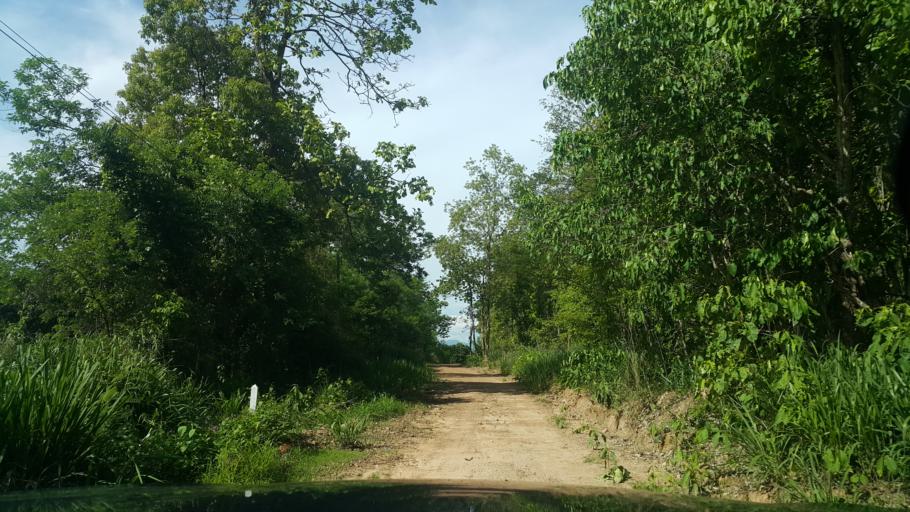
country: TH
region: Chiang Mai
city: Mae On
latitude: 18.7121
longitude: 99.2042
